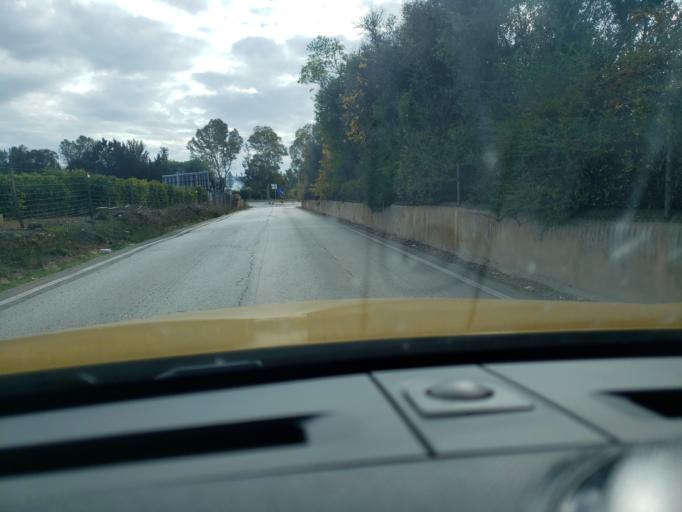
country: PT
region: Faro
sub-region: Portimao
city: Alvor
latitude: 37.1631
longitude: -8.5775
